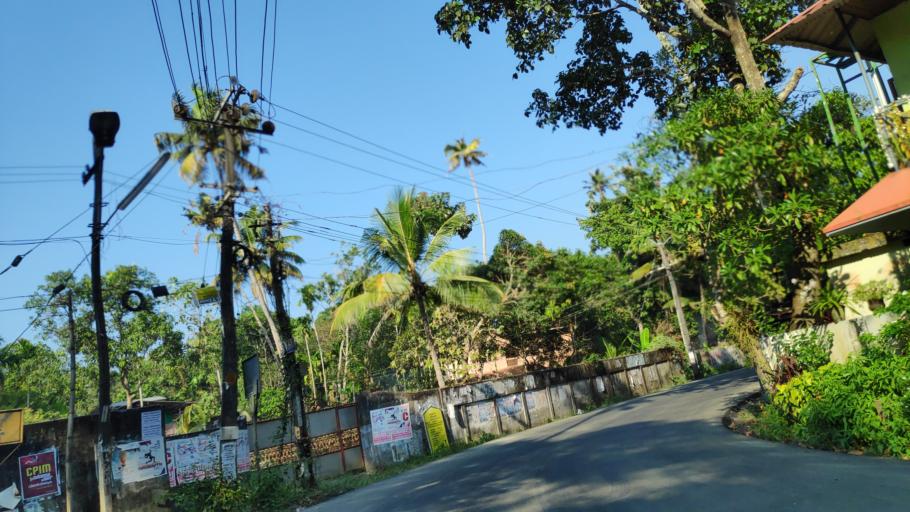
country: IN
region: Kerala
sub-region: Alappuzha
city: Alleppey
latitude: 9.5697
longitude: 76.3128
